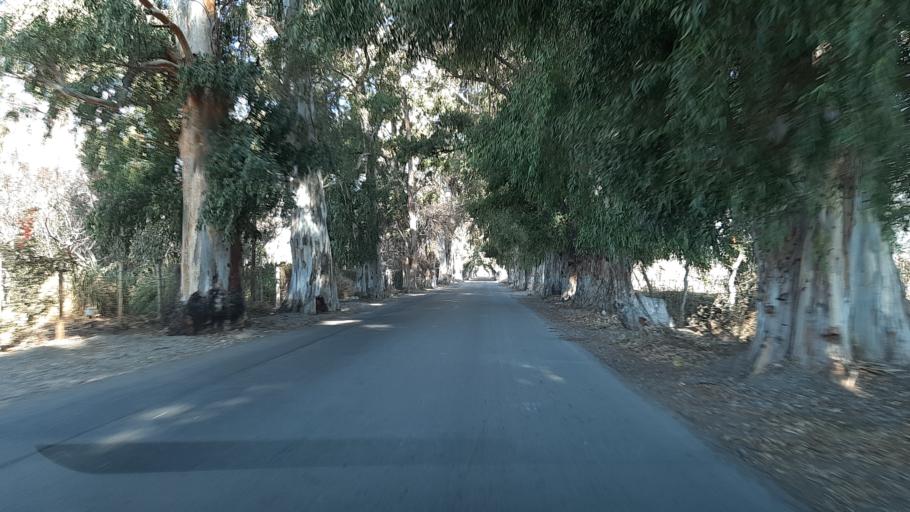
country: AR
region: San Juan
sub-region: Departamento de Zonda
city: Zonda
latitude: -31.5555
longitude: -68.7294
